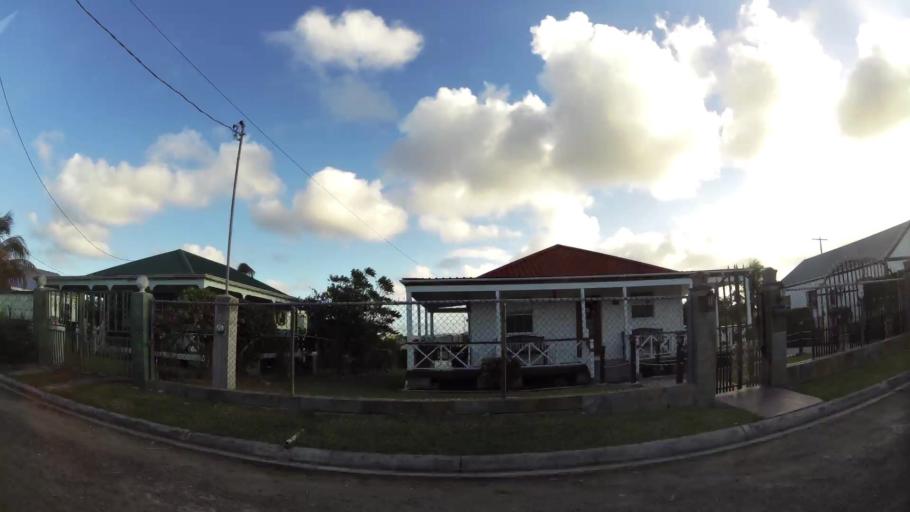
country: AG
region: Saint George
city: Piggotts
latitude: 17.1138
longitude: -61.7936
